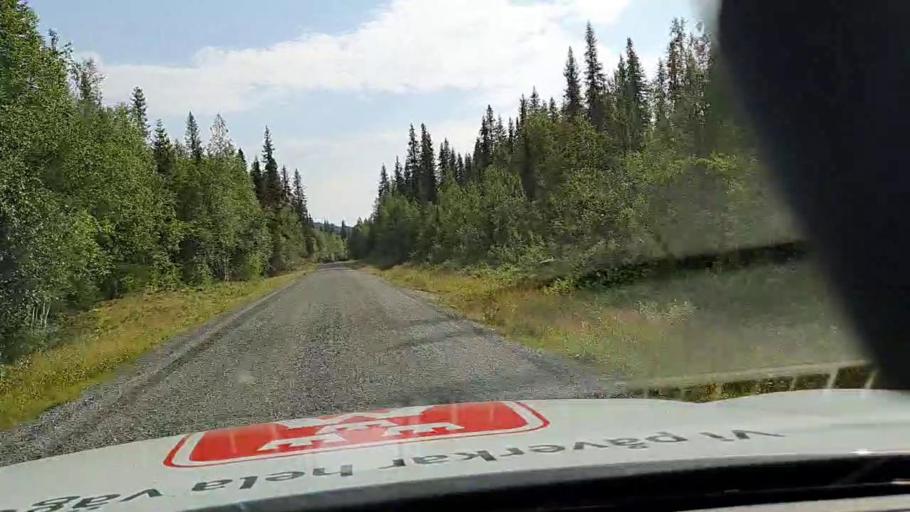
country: SE
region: Vaesterbotten
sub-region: Storumans Kommun
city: Fristad
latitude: 65.5396
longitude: 16.8018
